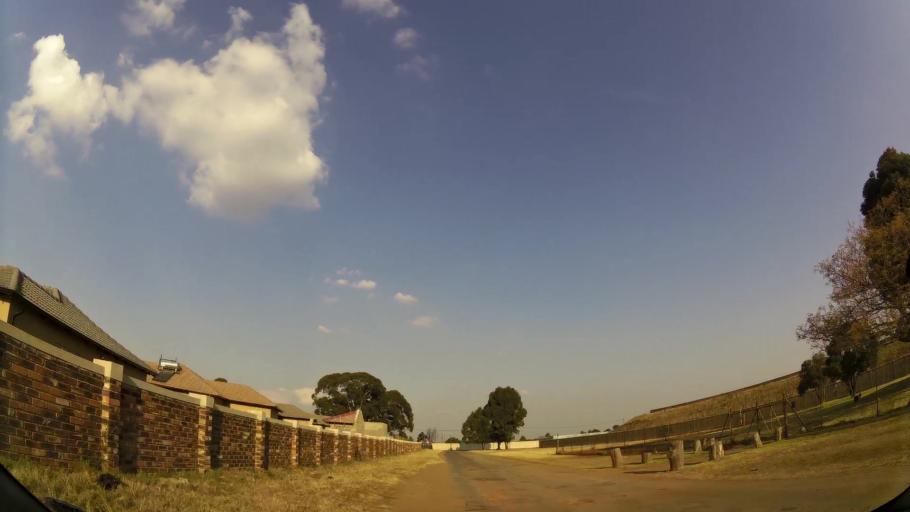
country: ZA
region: Gauteng
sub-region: Ekurhuleni Metropolitan Municipality
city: Benoni
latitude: -26.1417
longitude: 28.3737
